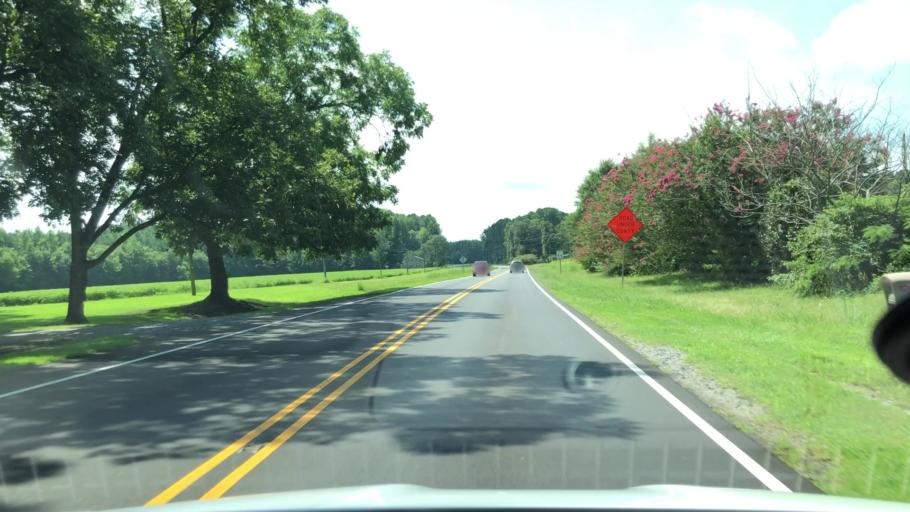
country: US
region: North Carolina
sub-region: Martin County
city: Williamston
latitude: 35.7399
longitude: -77.0757
